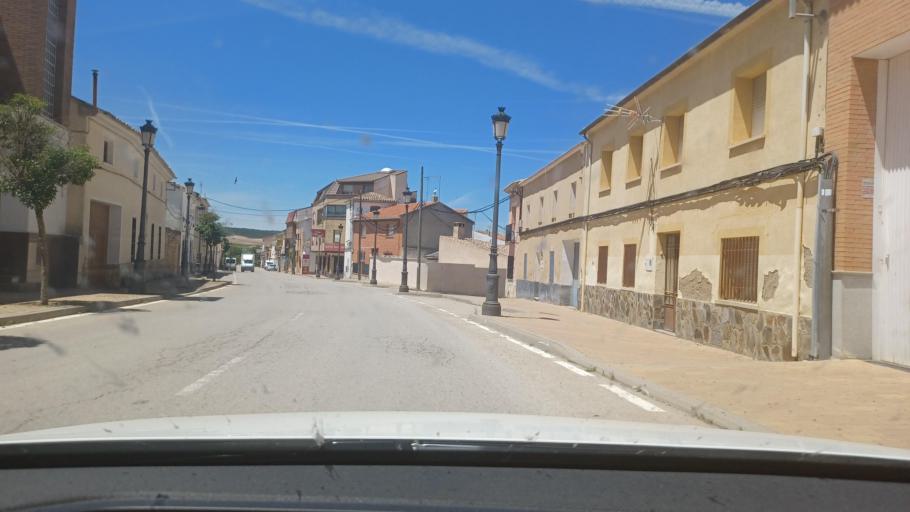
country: ES
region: Castille-La Mancha
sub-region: Provincia de Cuenca
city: Villares del Saz
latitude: 39.8391
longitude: -2.5033
